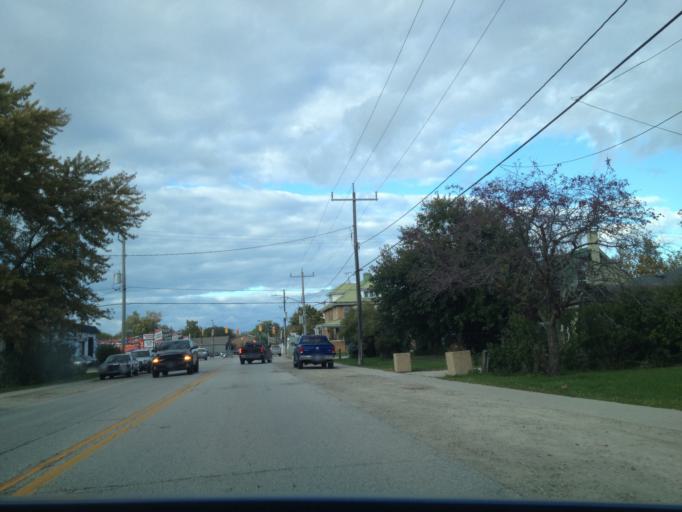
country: US
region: Michigan
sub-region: Wayne County
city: Grosse Pointe Farms
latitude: 42.2916
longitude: -82.7119
